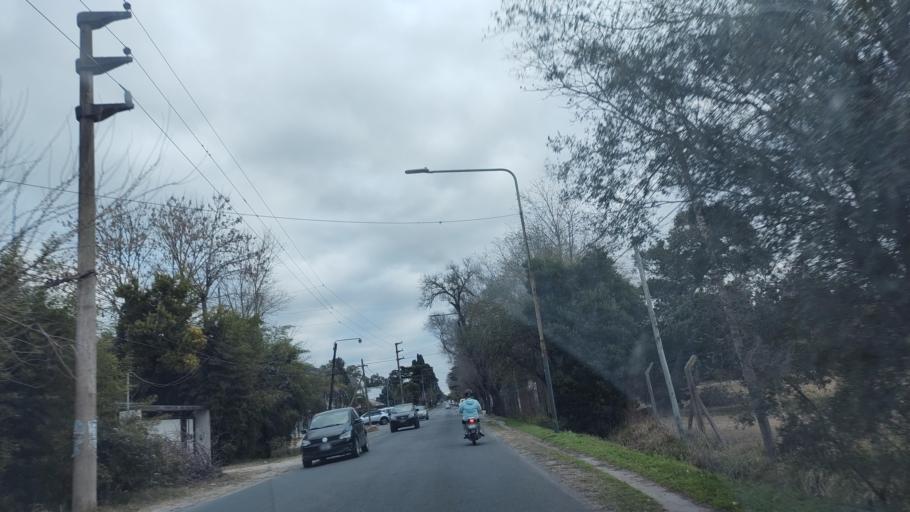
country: AR
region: Buenos Aires
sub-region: Partido de La Plata
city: La Plata
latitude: -34.8660
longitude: -58.0937
